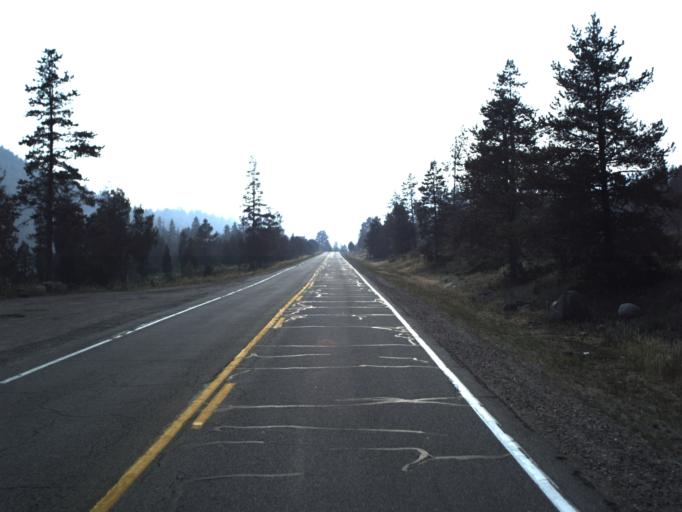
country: US
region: Utah
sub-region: Summit County
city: Francis
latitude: 40.5954
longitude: -111.0805
